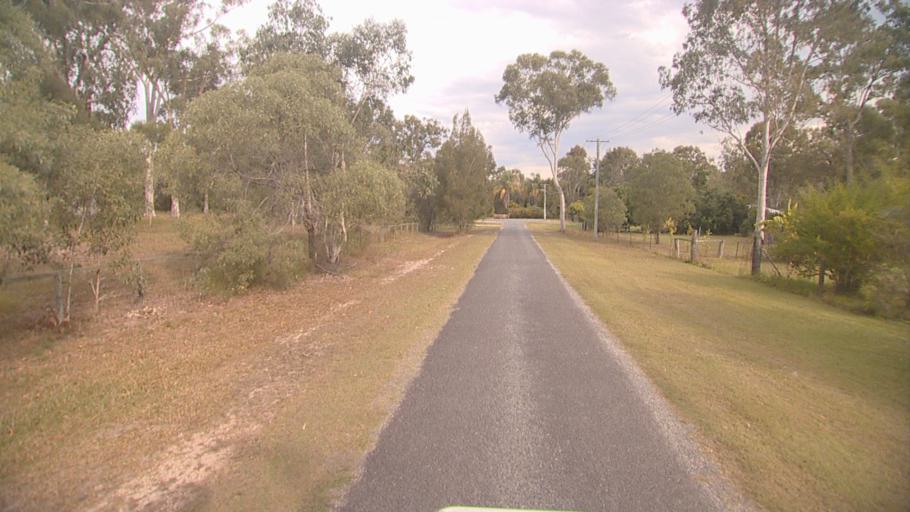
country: AU
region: Queensland
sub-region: Logan
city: Chambers Flat
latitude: -27.7758
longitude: 153.1137
